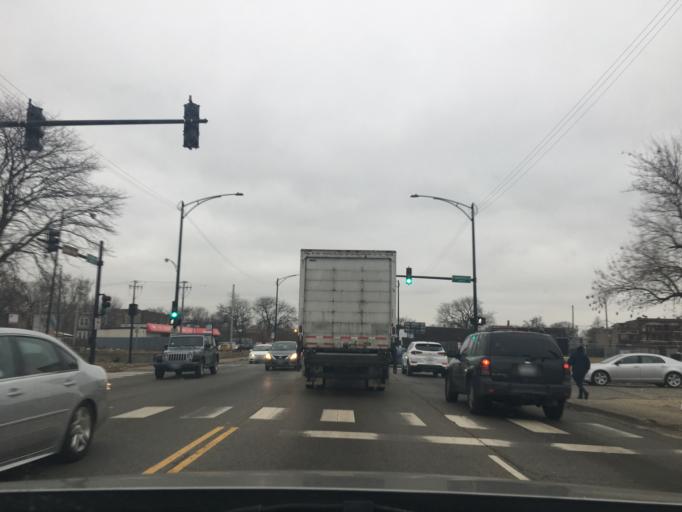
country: US
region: Illinois
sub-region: Cook County
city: Oak Park
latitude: 41.8847
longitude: -87.7455
